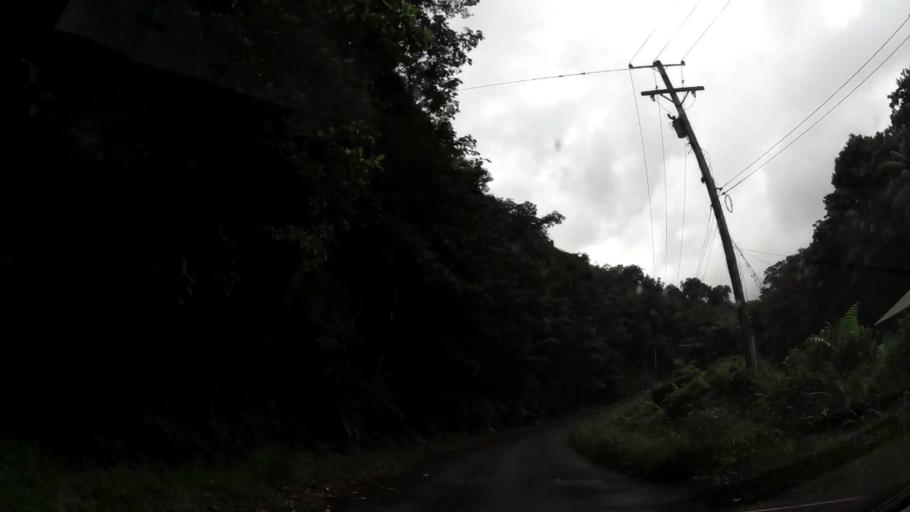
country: DM
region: Saint Paul
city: Pont Casse
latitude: 15.3959
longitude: -61.3106
